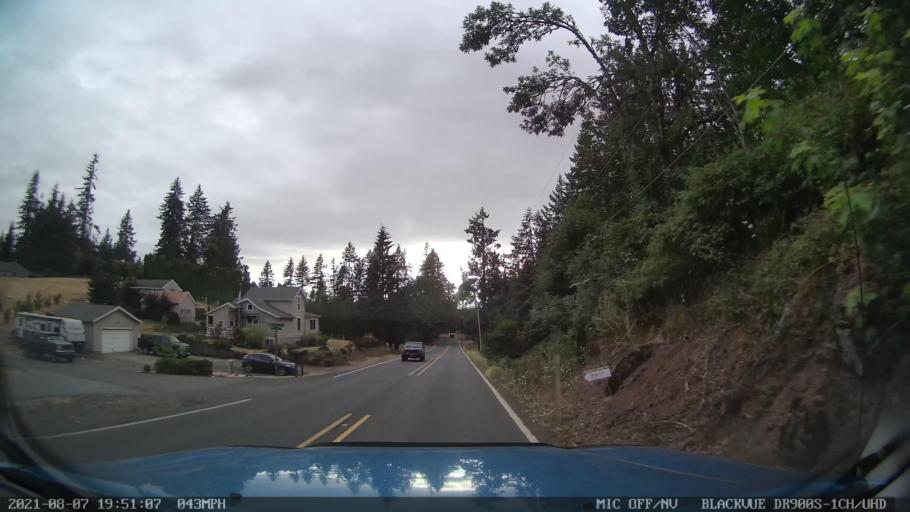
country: US
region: Oregon
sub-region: Marion County
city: Silverton
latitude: 44.9863
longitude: -122.7465
